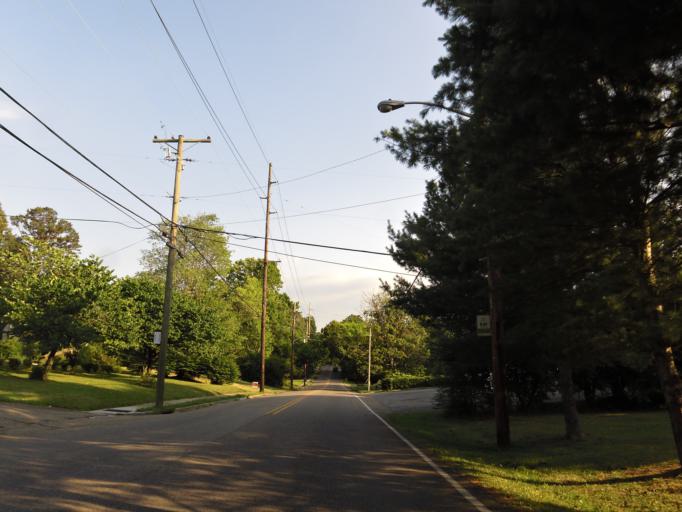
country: US
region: Tennessee
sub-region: Knox County
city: Knoxville
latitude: 36.0322
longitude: -83.9222
